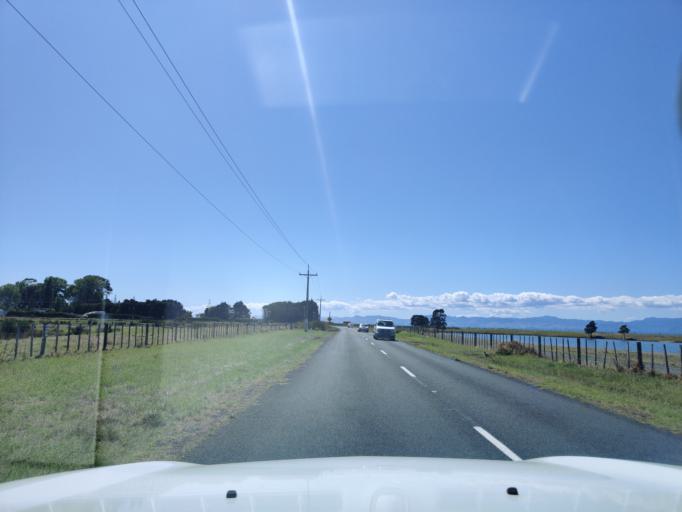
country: NZ
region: Waikato
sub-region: Thames-Coromandel District
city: Thames
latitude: -37.0567
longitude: 175.3006
